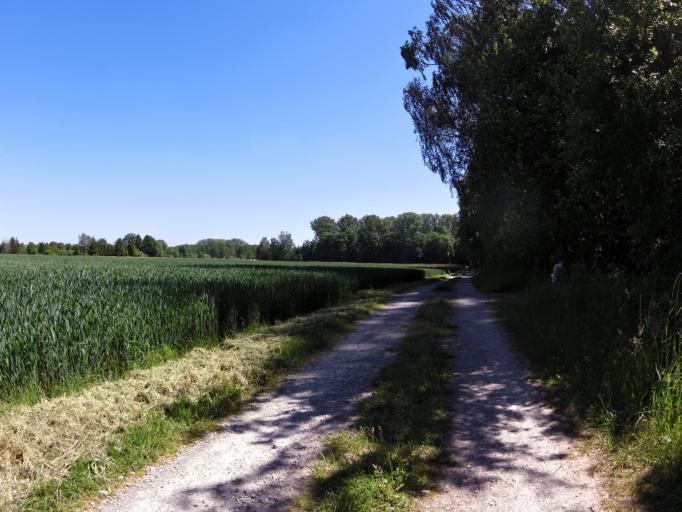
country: DE
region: Thuringia
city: Dankmarshausen
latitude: 50.9486
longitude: 10.0150
